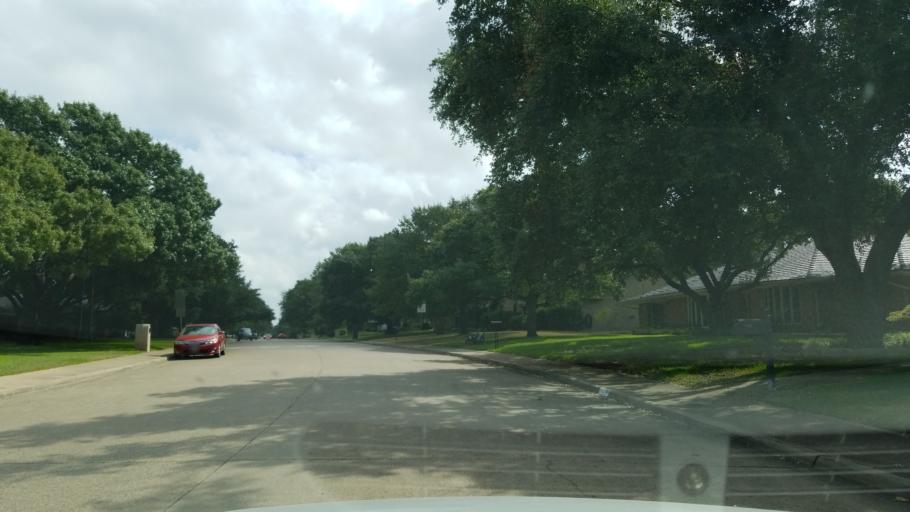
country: US
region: Texas
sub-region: Dallas County
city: Richardson
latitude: 32.9460
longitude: -96.7765
